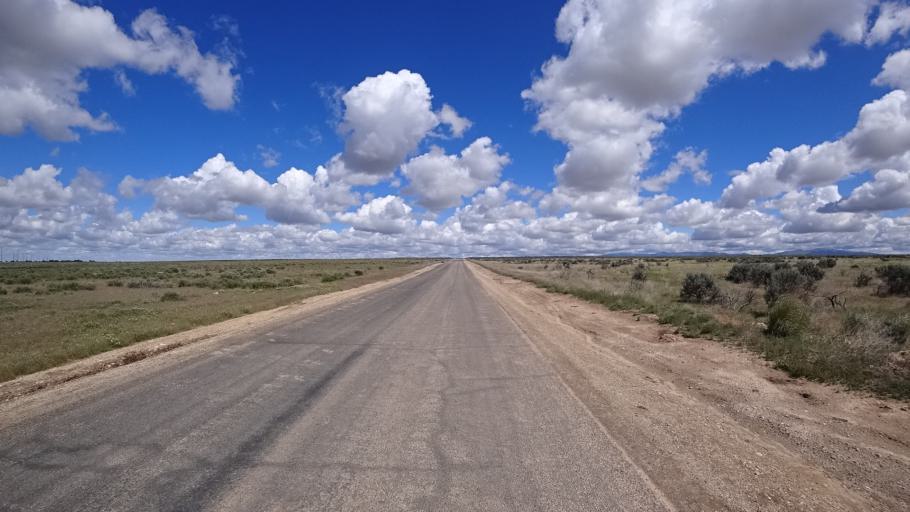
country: US
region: Idaho
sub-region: Ada County
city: Kuna
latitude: 43.4774
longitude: -116.2743
